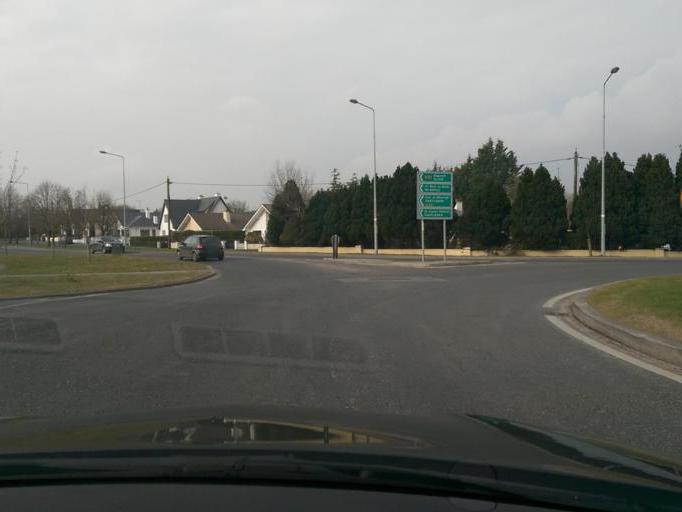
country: IE
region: Connaught
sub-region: Roscommon
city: Roscommon
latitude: 53.6339
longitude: -8.1821
